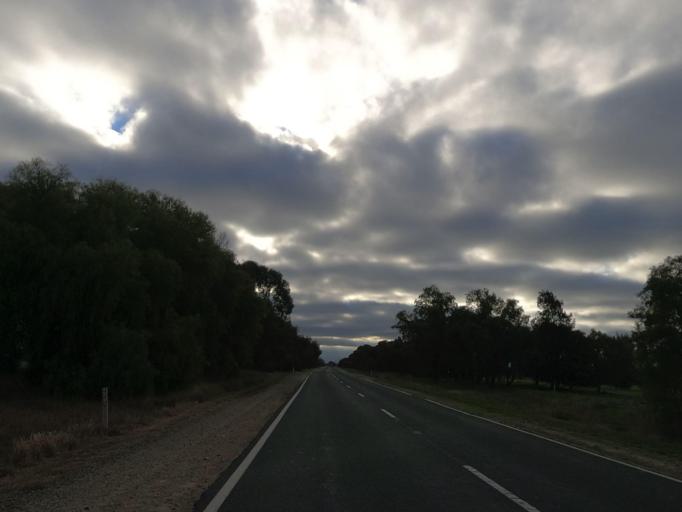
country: AU
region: Victoria
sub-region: Swan Hill
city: Swan Hill
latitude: -35.7974
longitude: 143.9527
